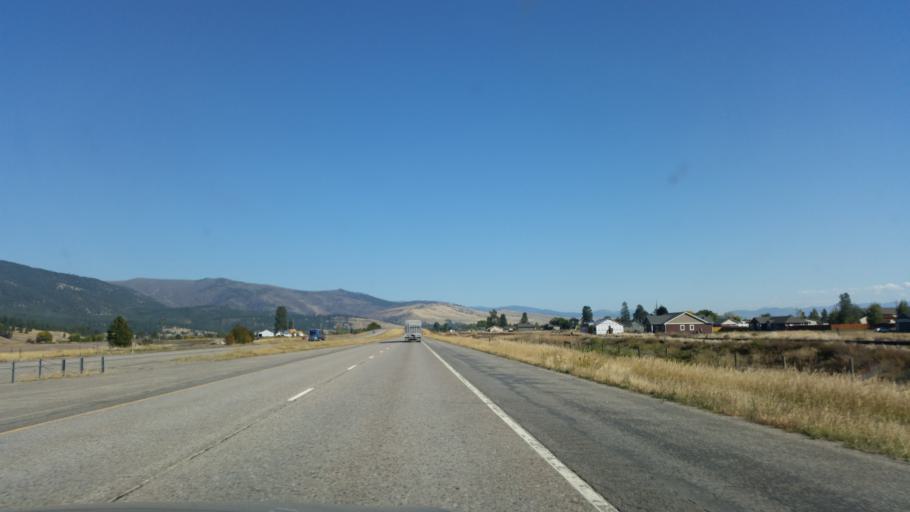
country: US
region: Montana
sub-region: Missoula County
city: Frenchtown
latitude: 47.0286
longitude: -114.3040
